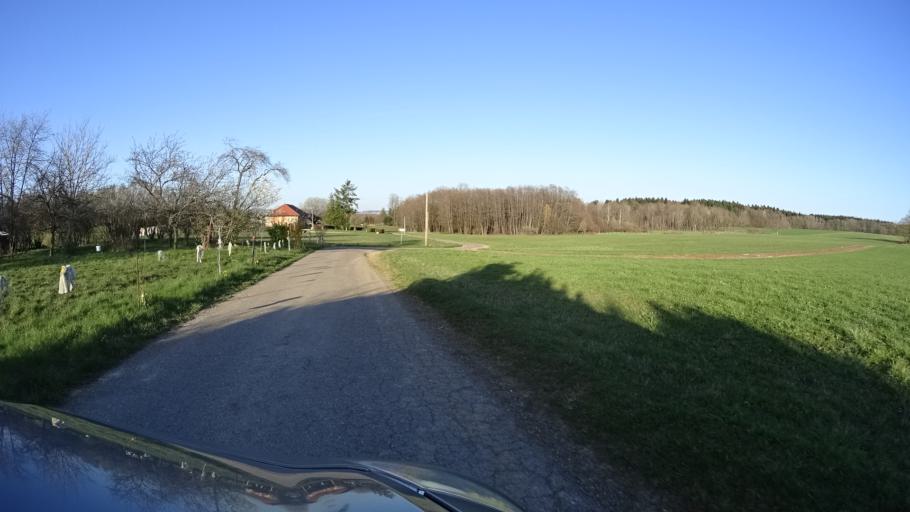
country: FR
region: Franche-Comte
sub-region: Departement du Doubs
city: Morre
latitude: 47.1950
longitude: 6.0563
